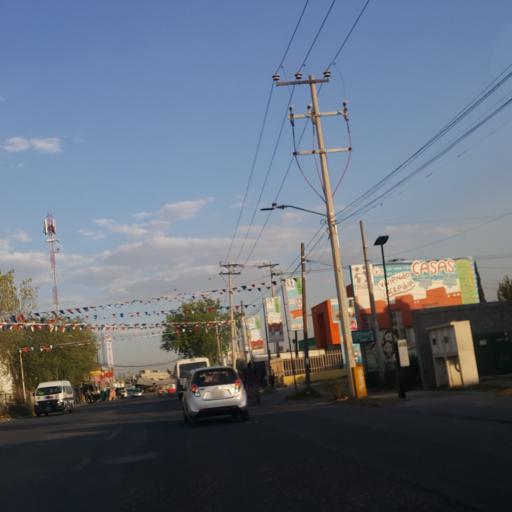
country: MX
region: Mexico
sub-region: Jaltenco
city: Alborada Jaltenco
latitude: 19.6575
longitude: -99.0745
